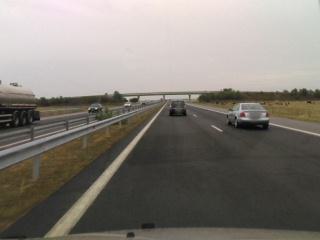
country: BG
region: Stara Zagora
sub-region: Obshtina Radnevo
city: Radnevo
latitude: 42.3742
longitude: 25.8154
